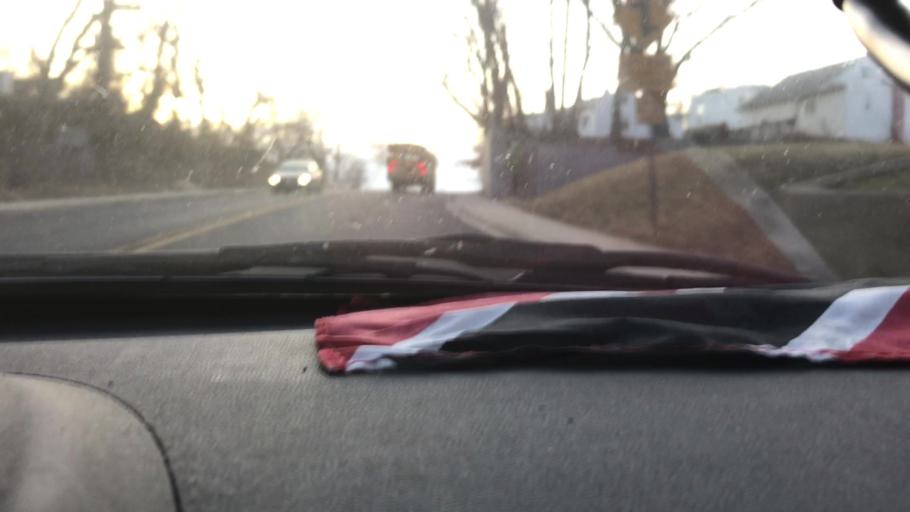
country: US
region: Maryland
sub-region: Prince George's County
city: Seat Pleasant
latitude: 38.8988
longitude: -76.9105
